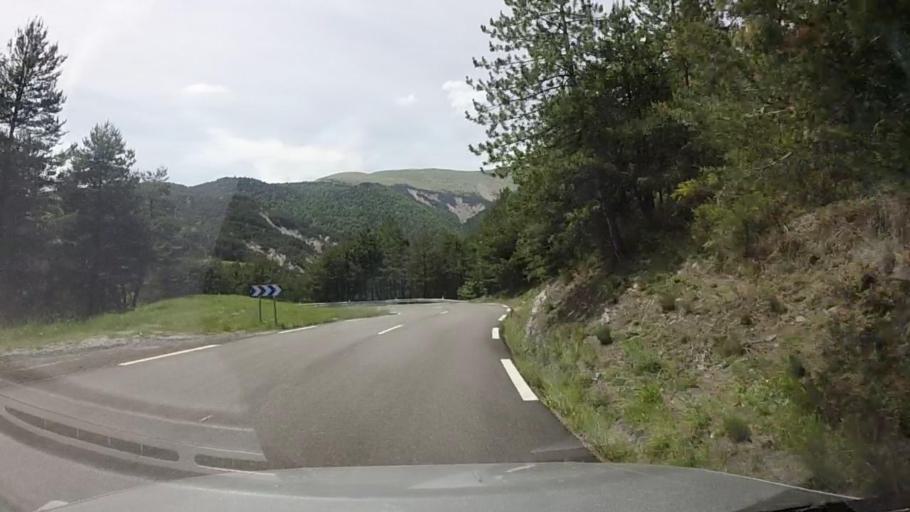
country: FR
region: Provence-Alpes-Cote d'Azur
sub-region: Departement des Alpes-de-Haute-Provence
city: Le Brusquet
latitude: 44.2391
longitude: 6.3593
